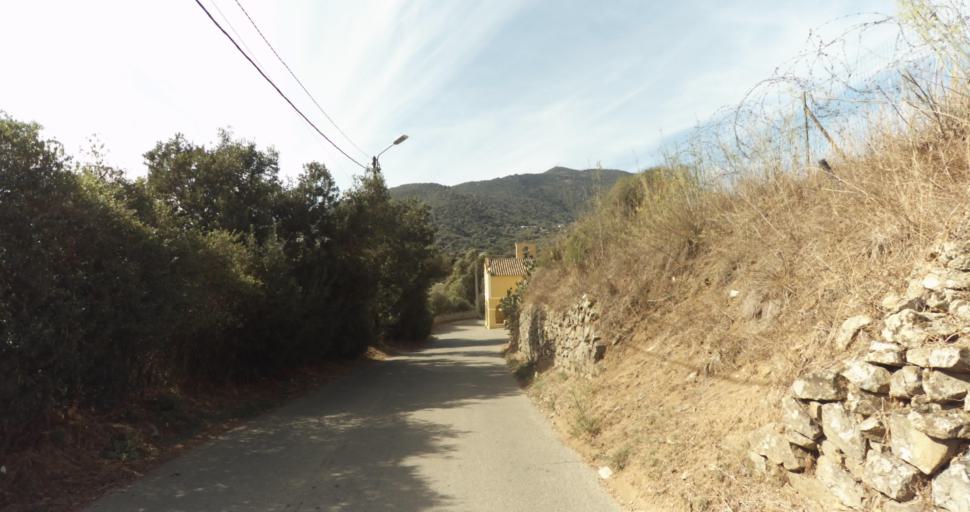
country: FR
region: Corsica
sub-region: Departement de la Corse-du-Sud
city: Ajaccio
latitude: 41.9311
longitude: 8.7296
